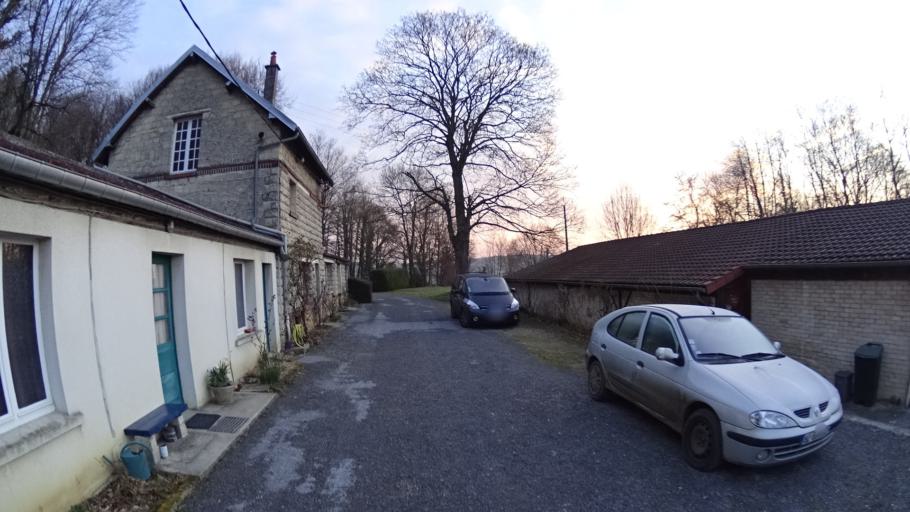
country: FR
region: Picardie
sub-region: Departement de l'Aisne
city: Vic-sur-Aisne
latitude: 49.4381
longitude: 3.1298
